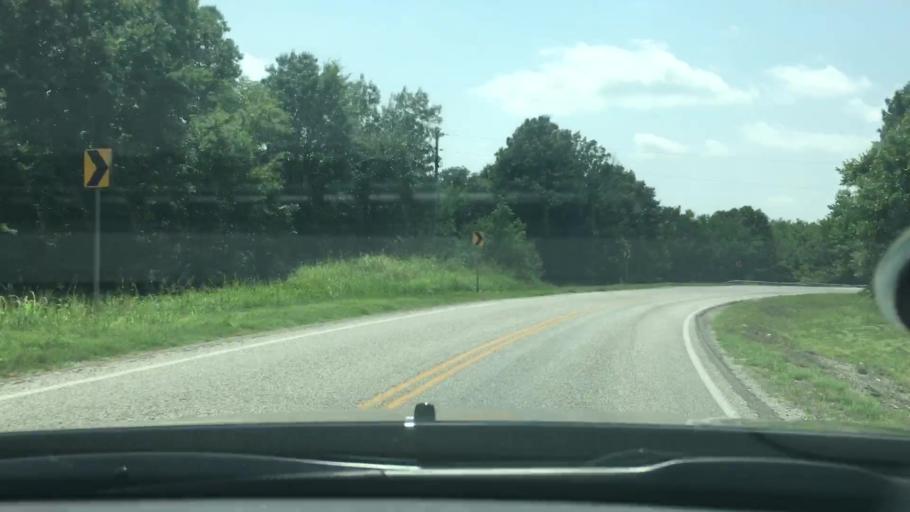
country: US
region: Oklahoma
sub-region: Johnston County
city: Tishomingo
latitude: 34.3729
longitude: -96.4565
